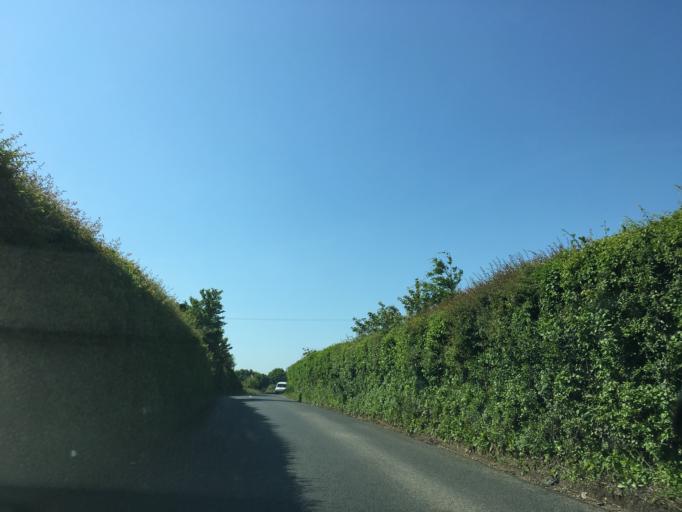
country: GB
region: England
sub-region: Isle of Wight
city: Ryde
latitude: 50.7047
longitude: -1.1669
